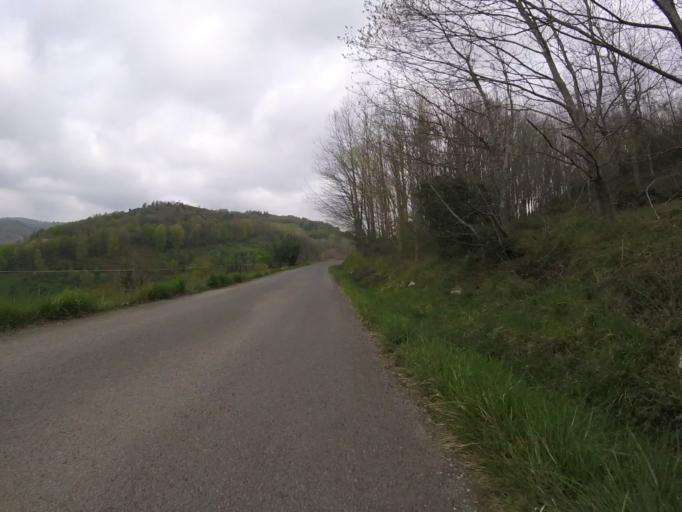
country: ES
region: Basque Country
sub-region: Provincia de Guipuzcoa
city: Zizurkil
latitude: 43.2119
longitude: -2.0844
